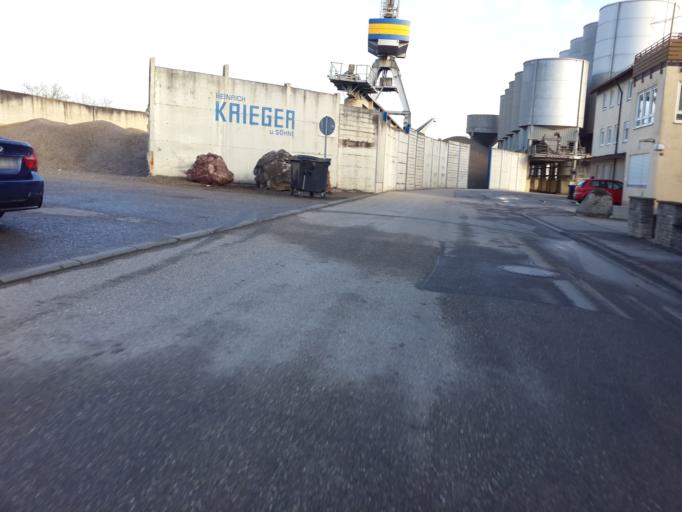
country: DE
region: Baden-Wuerttemberg
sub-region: Regierungsbezirk Stuttgart
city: Neckarsulm
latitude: 49.1980
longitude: 9.2175
